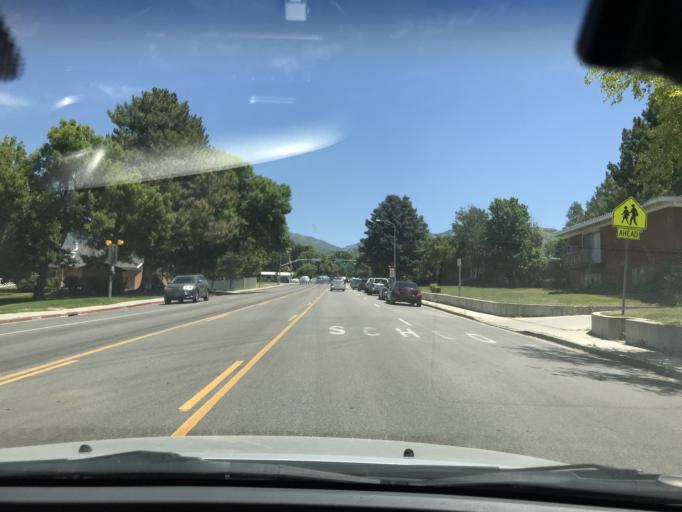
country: US
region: Utah
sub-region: Davis County
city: Woods Cross
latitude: 40.8616
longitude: -111.8875
